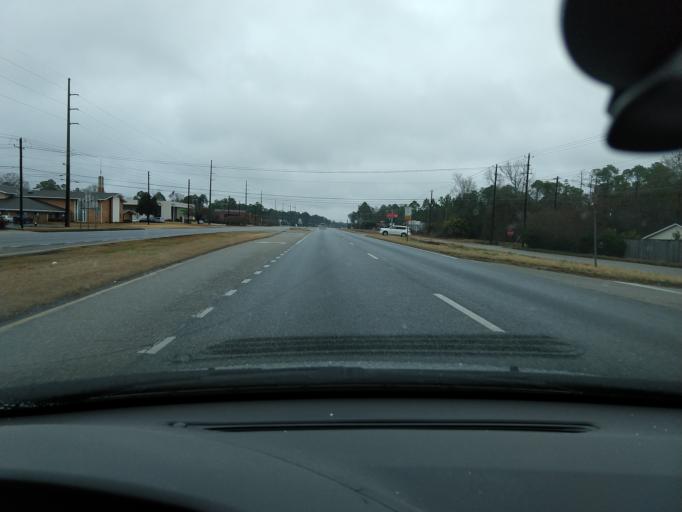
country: US
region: Alabama
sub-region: Houston County
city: Dothan
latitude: 31.2320
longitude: -85.4319
